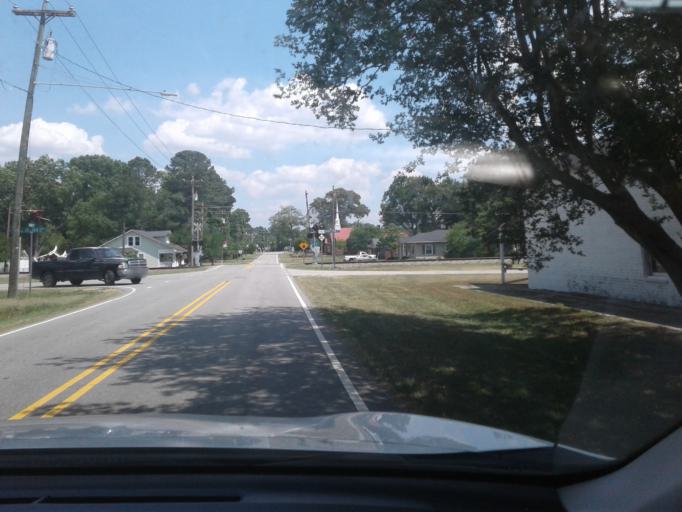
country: US
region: North Carolina
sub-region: Harnett County
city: Erwin
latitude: 35.2180
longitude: -78.6813
